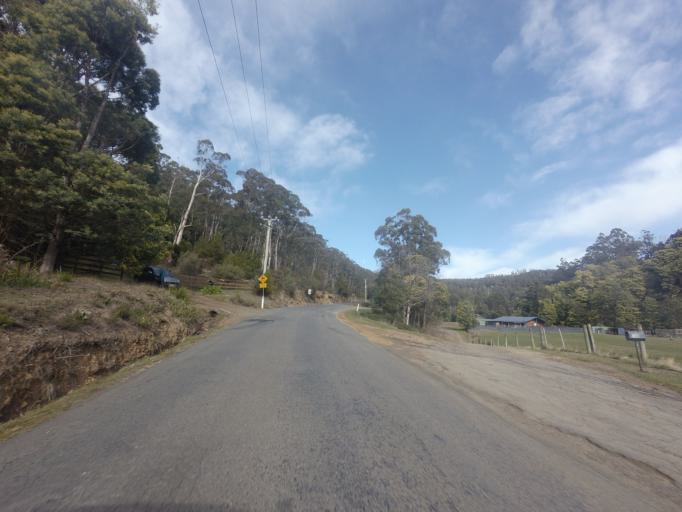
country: AU
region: Tasmania
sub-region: Kingborough
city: Margate
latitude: -42.9997
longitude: 147.1776
